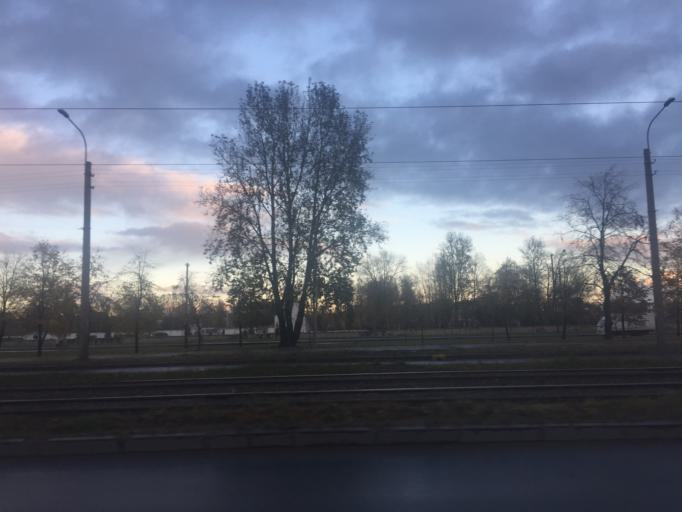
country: RU
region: St.-Petersburg
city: Obukhovo
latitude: 59.8870
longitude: 30.4646
